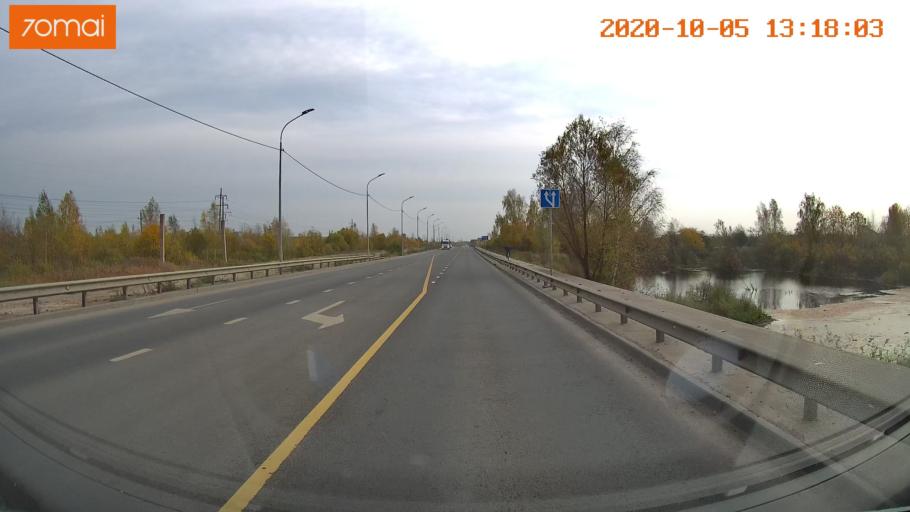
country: RU
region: Ivanovo
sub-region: Gorod Ivanovo
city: Ivanovo
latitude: 56.9807
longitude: 40.9161
